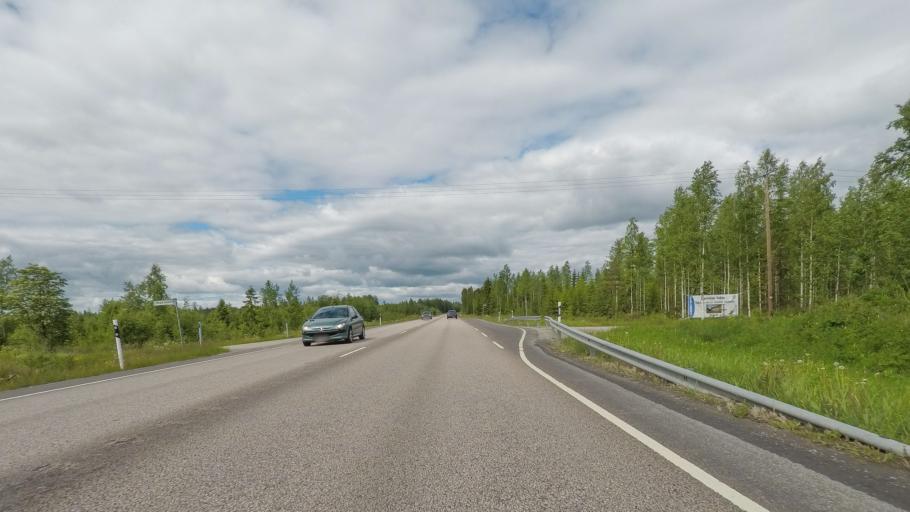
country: FI
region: Paijanne Tavastia
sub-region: Lahti
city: Hartola
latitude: 61.5869
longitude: 26.0094
